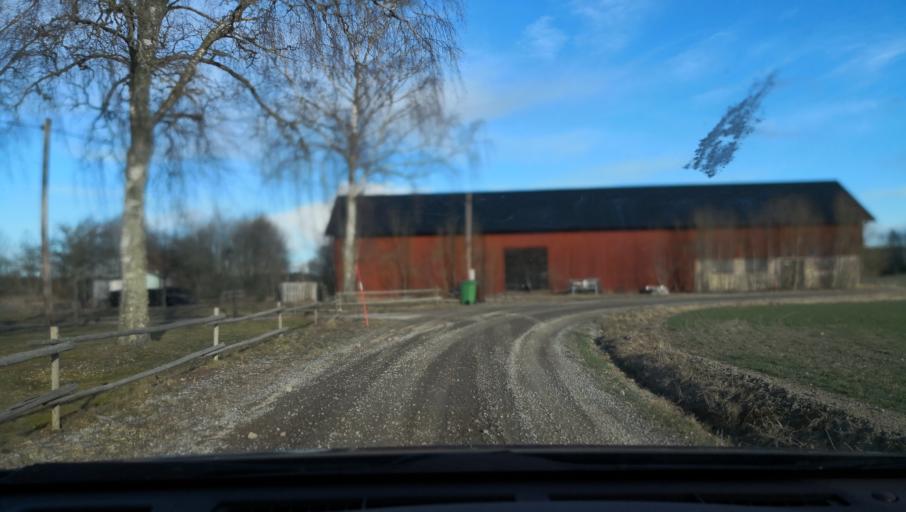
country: SE
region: Vaestmanland
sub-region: Arboga Kommun
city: Arboga
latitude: 59.4456
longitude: 15.7519
